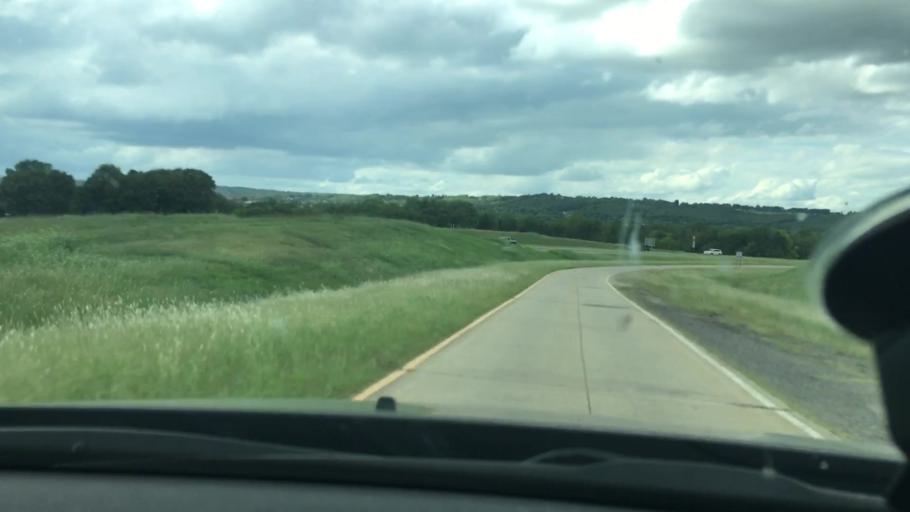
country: US
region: Oklahoma
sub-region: Okmulgee County
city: Henryetta
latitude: 35.4335
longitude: -95.9694
